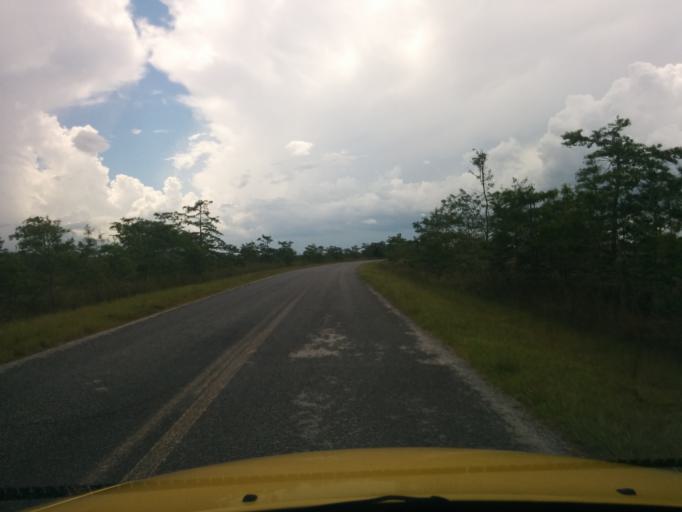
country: US
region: Florida
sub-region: Miami-Dade County
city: Florida City
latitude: 25.4324
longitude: -80.7778
